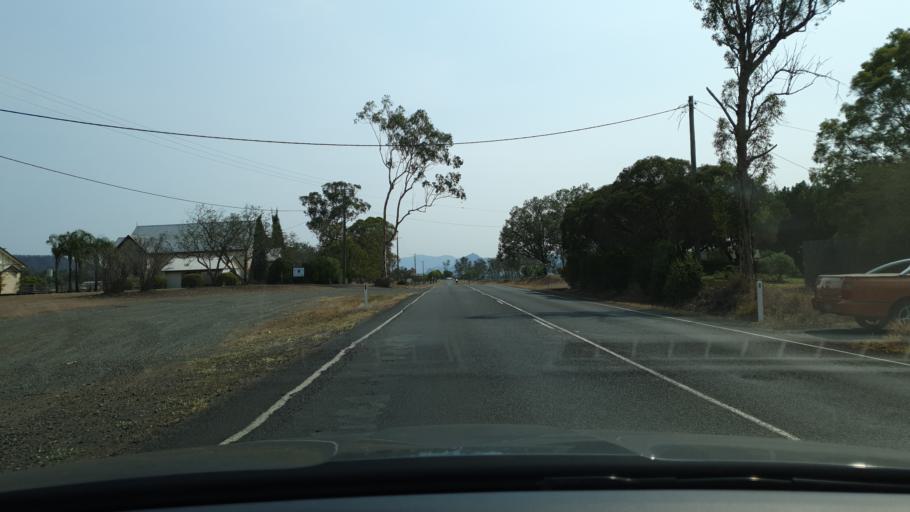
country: AU
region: Queensland
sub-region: Ipswich
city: Deebing Heights
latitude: -28.0128
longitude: 152.6761
